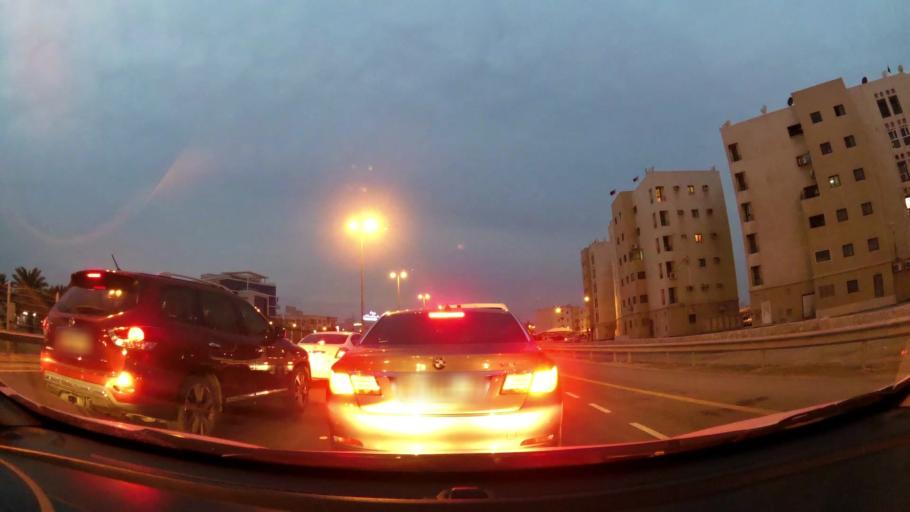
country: BH
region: Northern
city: Madinat `Isa
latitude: 26.1801
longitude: 50.5384
